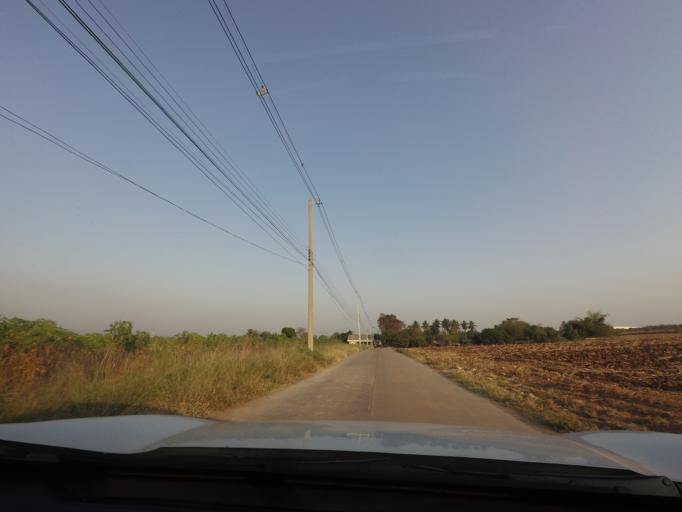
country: TH
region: Nakhon Ratchasima
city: Pak Chong
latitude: 14.6466
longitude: 101.3987
